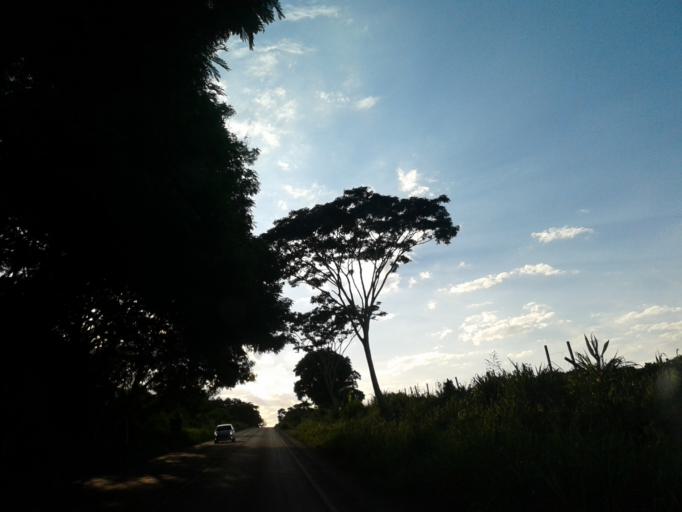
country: BR
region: Minas Gerais
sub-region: Capinopolis
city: Capinopolis
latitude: -18.6756
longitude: -49.5620
